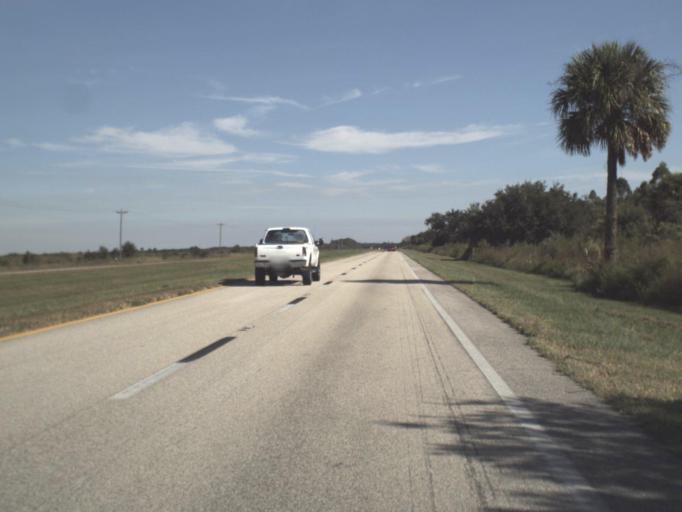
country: US
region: Florida
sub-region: Glades County
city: Moore Haven
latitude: 26.9100
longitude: -81.2730
